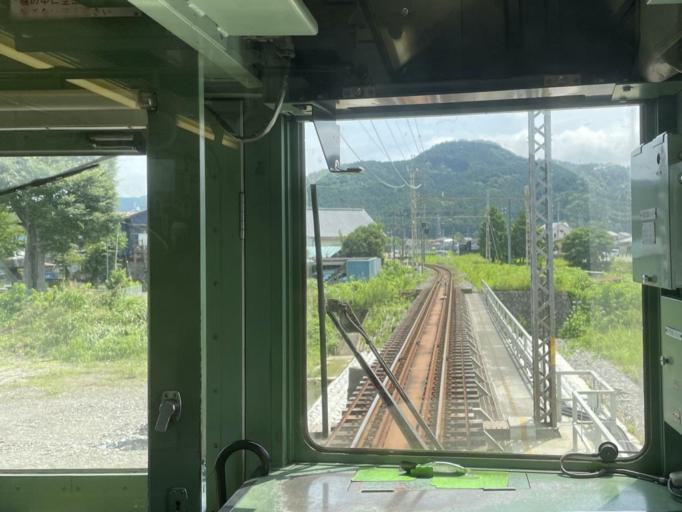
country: JP
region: Tochigi
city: Tanuma
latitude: 36.3975
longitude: 139.6069
